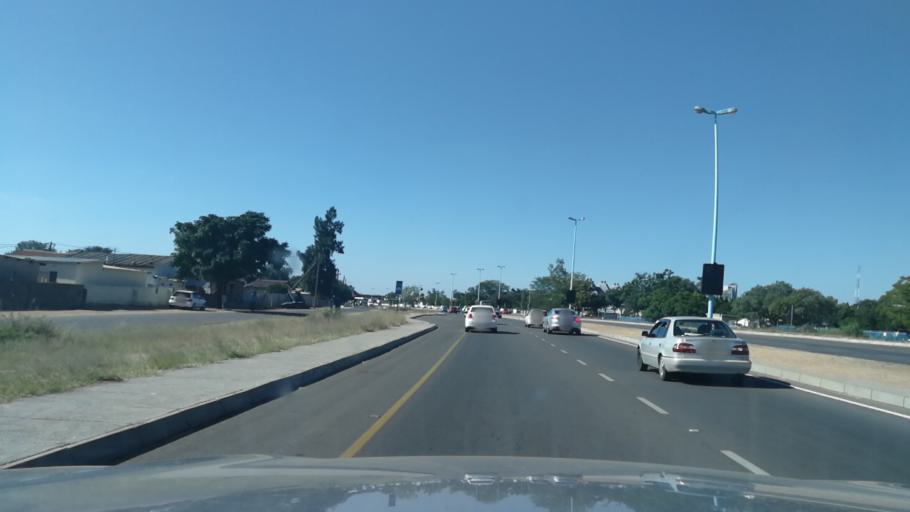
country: BW
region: South East
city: Gaborone
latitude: -24.6806
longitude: 25.9149
